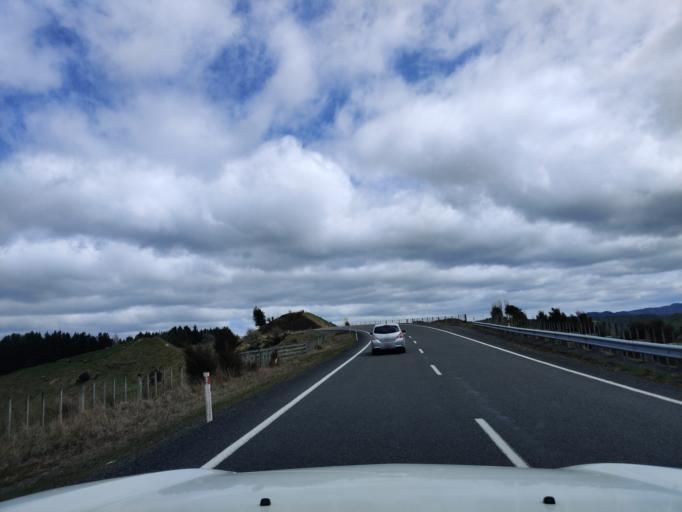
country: NZ
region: Manawatu-Wanganui
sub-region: Wanganui District
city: Wanganui
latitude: -39.7856
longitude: 175.2208
